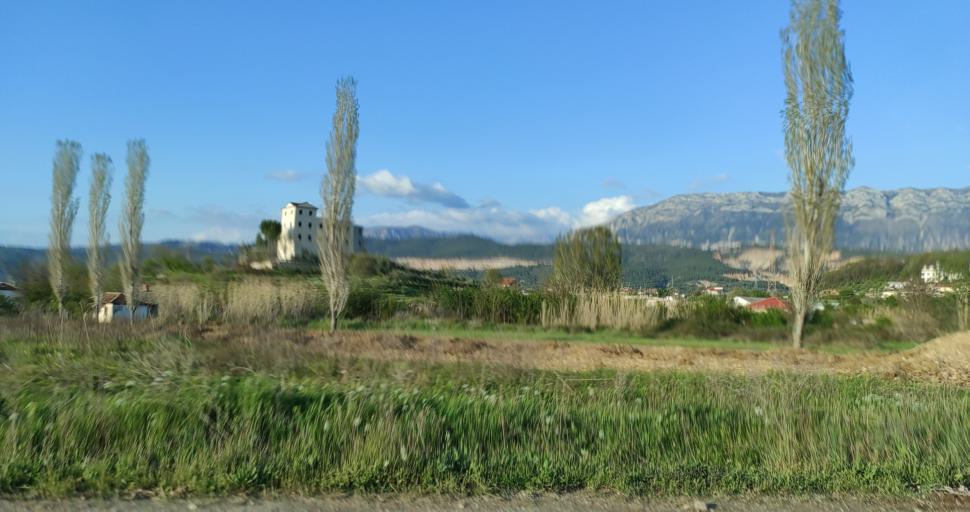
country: AL
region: Durres
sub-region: Rrethi i Krujes
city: Fushe-Kruje
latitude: 41.4848
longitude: 19.7317
